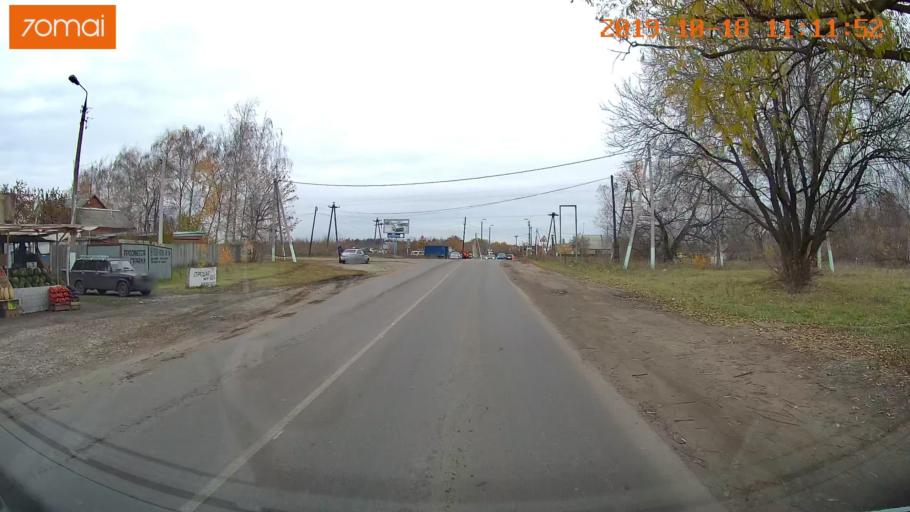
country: RU
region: Tula
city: Kimovsk
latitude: 53.9622
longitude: 38.5518
